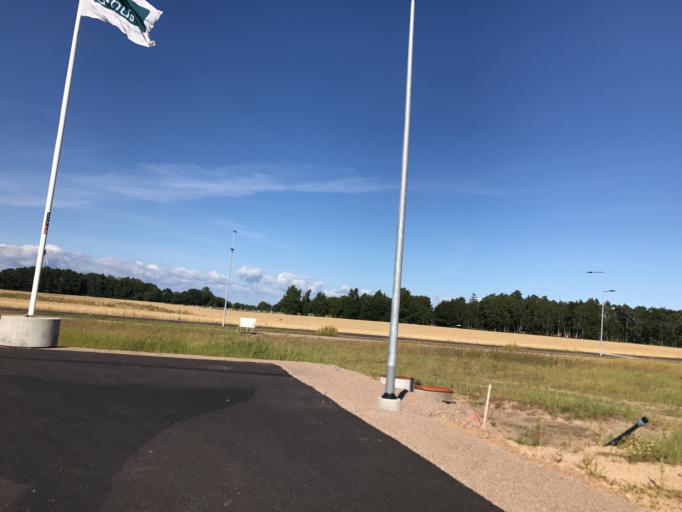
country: SE
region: Skane
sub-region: Bastads Kommun
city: Bastad
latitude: 56.4344
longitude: 12.9042
